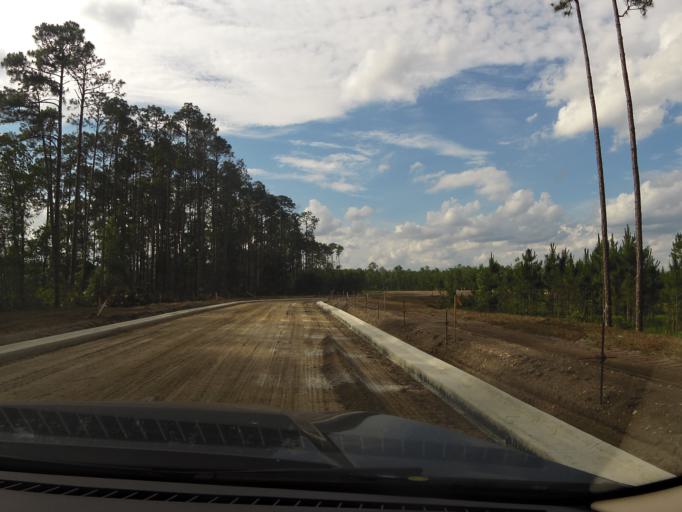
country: US
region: Florida
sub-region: Saint Johns County
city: Palm Valley
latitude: 30.1837
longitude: -81.5119
